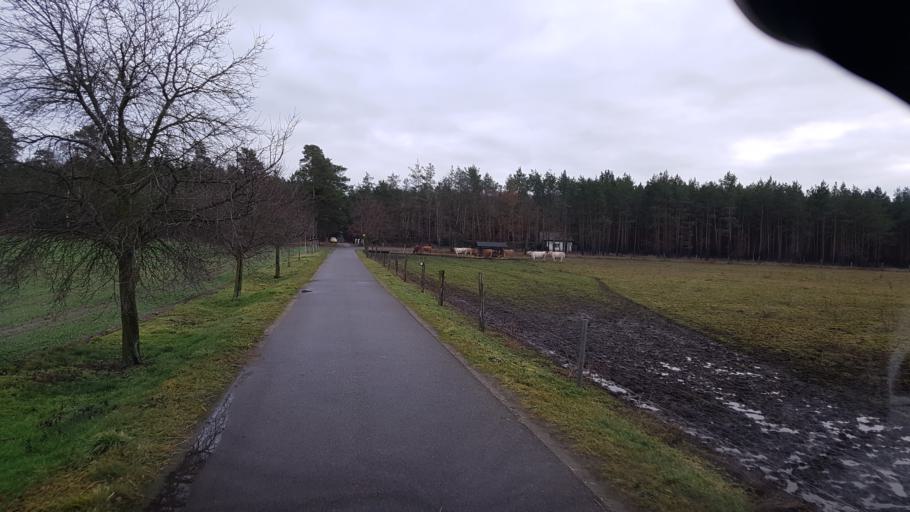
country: DE
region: Brandenburg
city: Altdobern
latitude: 51.6810
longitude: 14.0204
